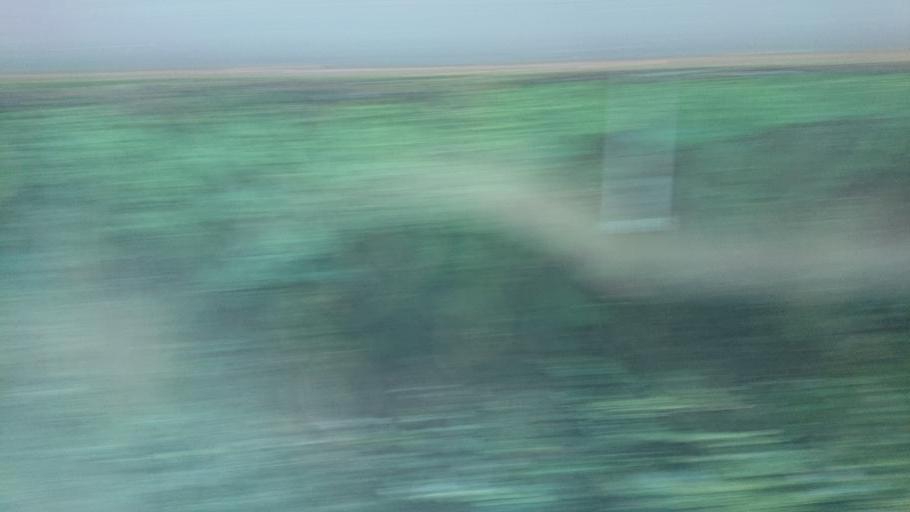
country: TW
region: Taiwan
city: Lugu
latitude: 23.5070
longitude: 120.7977
